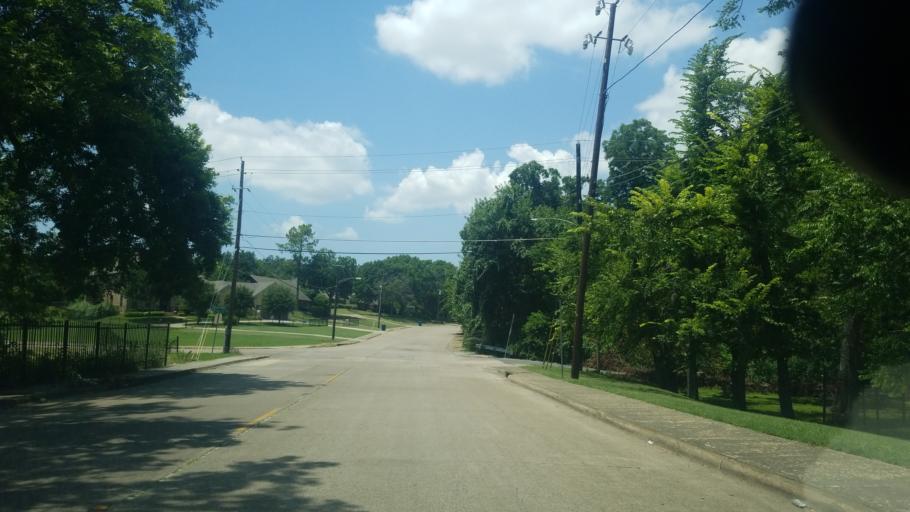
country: US
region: Texas
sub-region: Dallas County
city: Dallas
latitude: 32.7267
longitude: -96.7899
